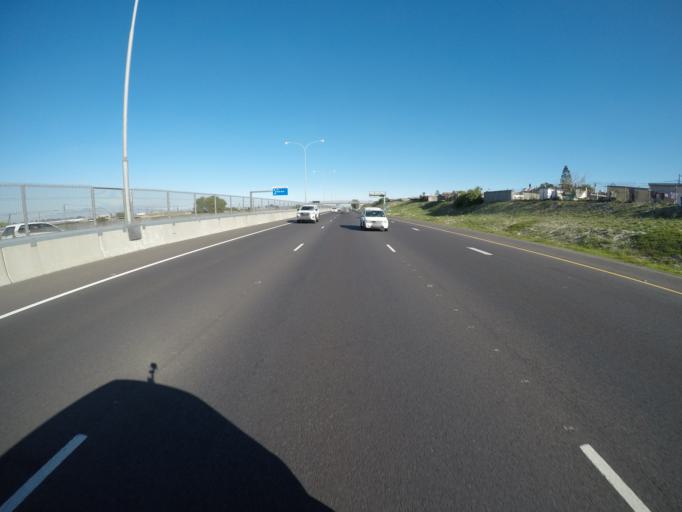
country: ZA
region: Western Cape
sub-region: City of Cape Town
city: Kraaifontein
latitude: -33.9649
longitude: 18.6552
